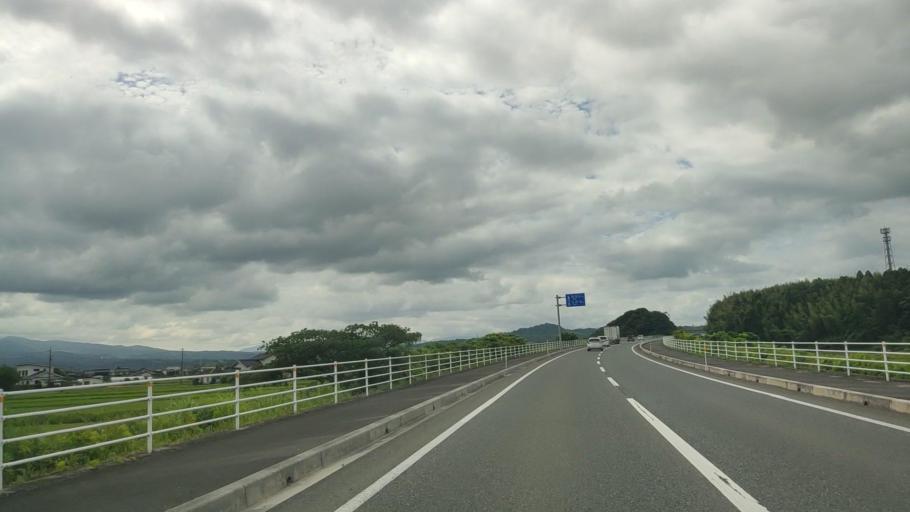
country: JP
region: Tottori
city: Yonago
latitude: 35.3958
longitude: 133.3810
